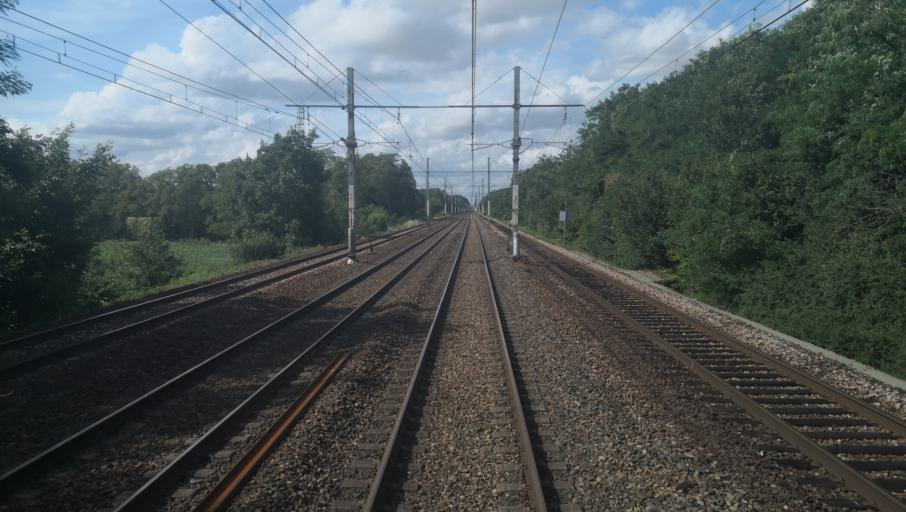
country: FR
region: Ile-de-France
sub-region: Departement de l'Essonne
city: Cheptainville
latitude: 48.5416
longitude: 2.2932
